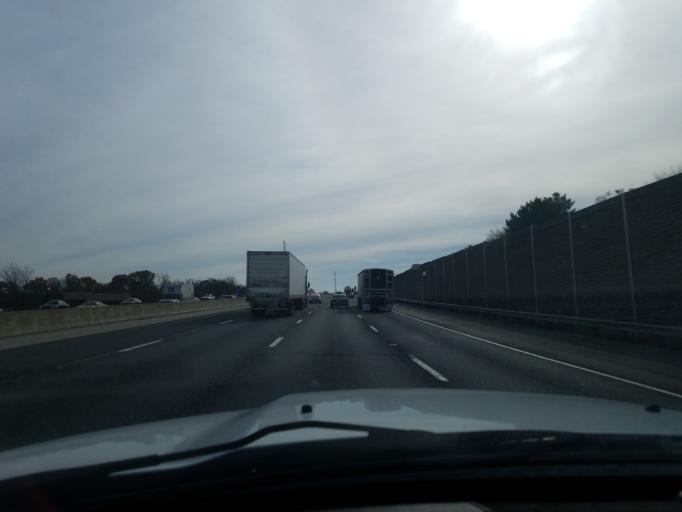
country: US
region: Indiana
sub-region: Marion County
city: Lawrence
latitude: 39.8868
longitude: -86.0478
